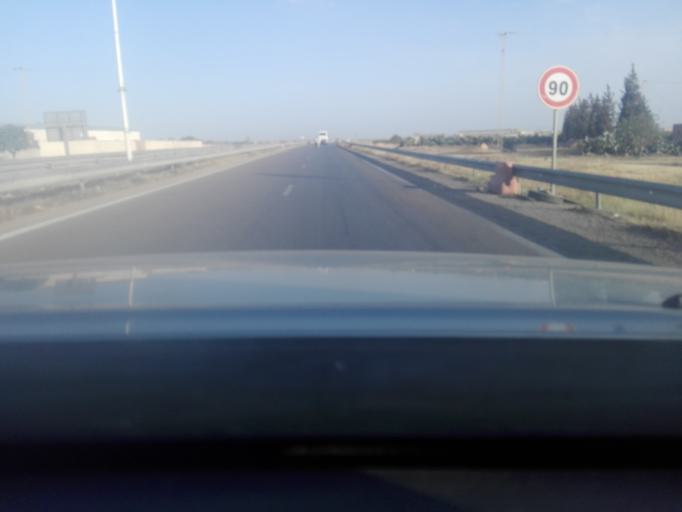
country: TN
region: Safaqis
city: Al Qarmadah
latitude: 34.8573
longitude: 10.7583
